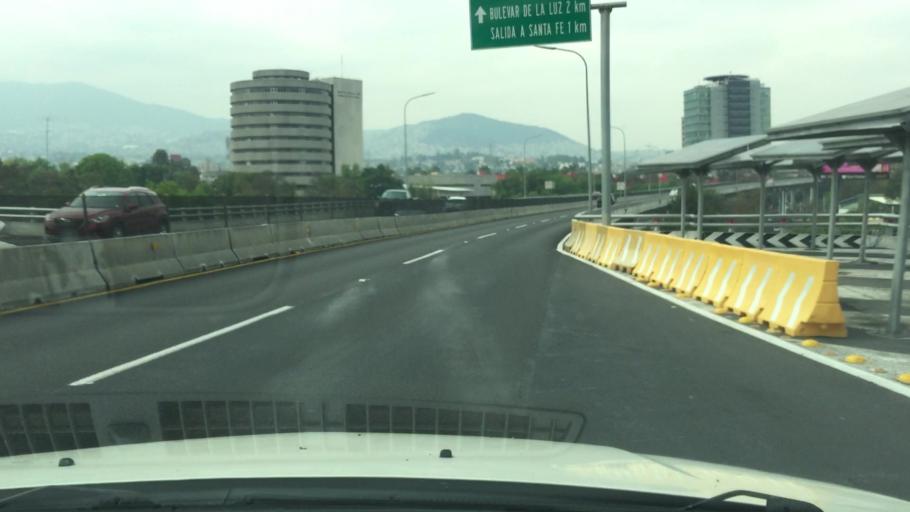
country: MX
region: Mexico City
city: Magdalena Contreras
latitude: 19.3078
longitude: -99.2156
